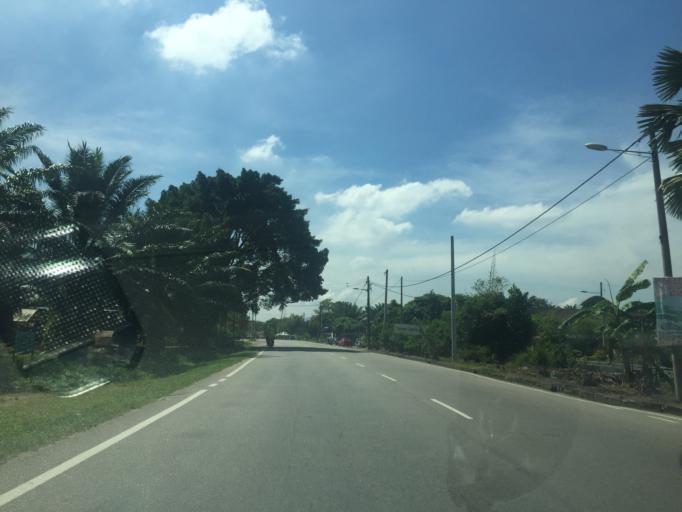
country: MY
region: Penang
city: Tasek Glugor
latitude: 5.4855
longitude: 100.5040
